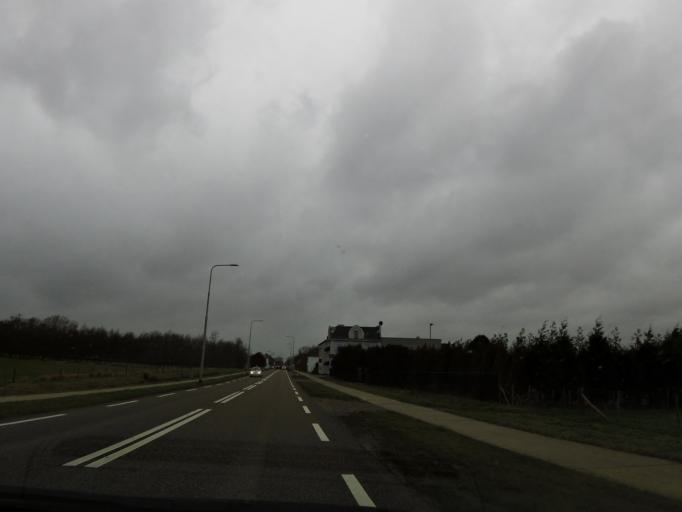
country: NL
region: Limburg
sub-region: Gemeente Vaals
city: Vaals
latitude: 50.7826
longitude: 5.9984
